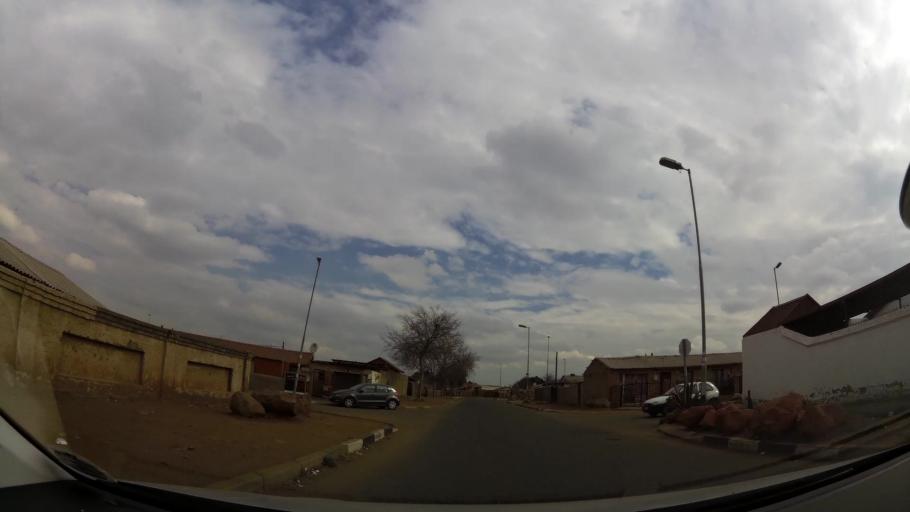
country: ZA
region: Gauteng
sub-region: City of Johannesburg Metropolitan Municipality
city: Soweto
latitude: -26.2677
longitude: 27.8583
